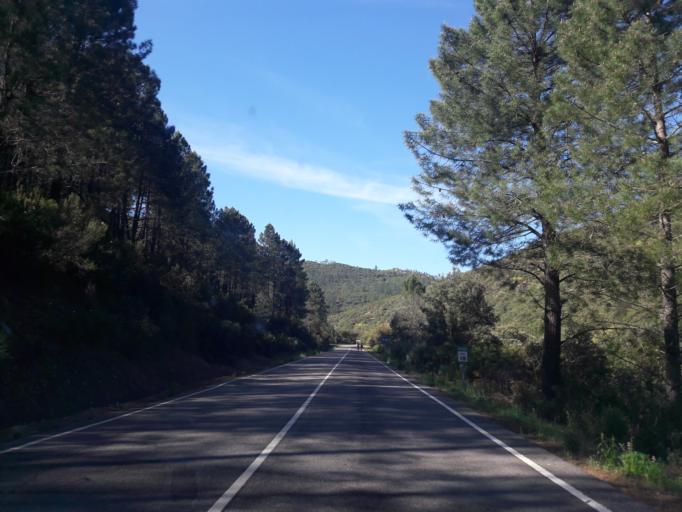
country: ES
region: Castille and Leon
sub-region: Provincia de Salamanca
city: Sotoserrano
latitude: 40.4138
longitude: -6.0525
